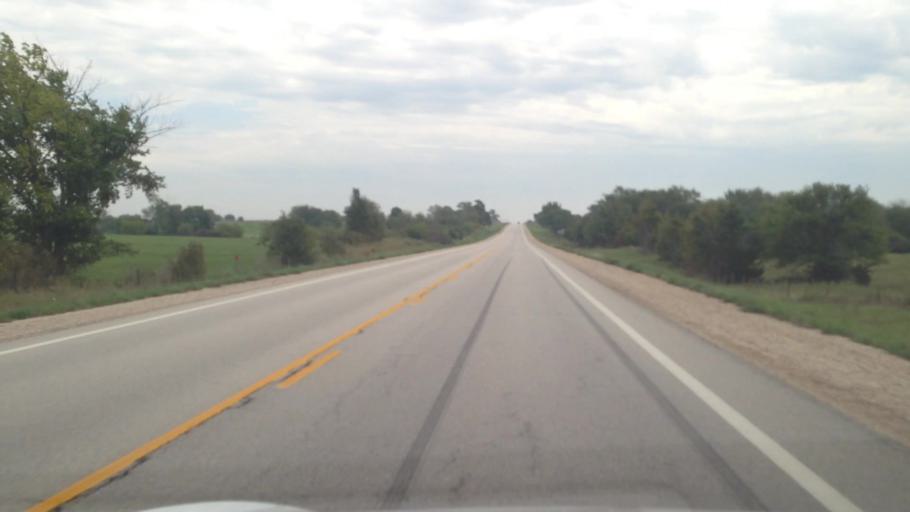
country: US
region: Kansas
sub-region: Anderson County
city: Garnett
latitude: 38.0818
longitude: -95.2368
